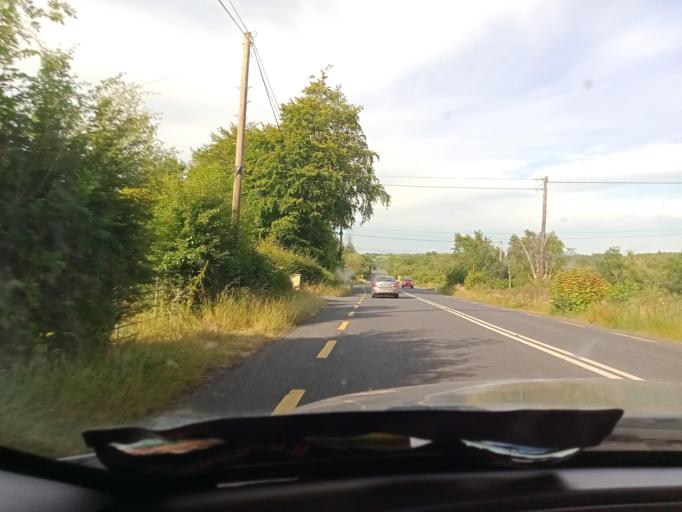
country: IE
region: Ulster
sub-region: An Cabhan
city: Cavan
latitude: 53.9401
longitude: -7.3909
